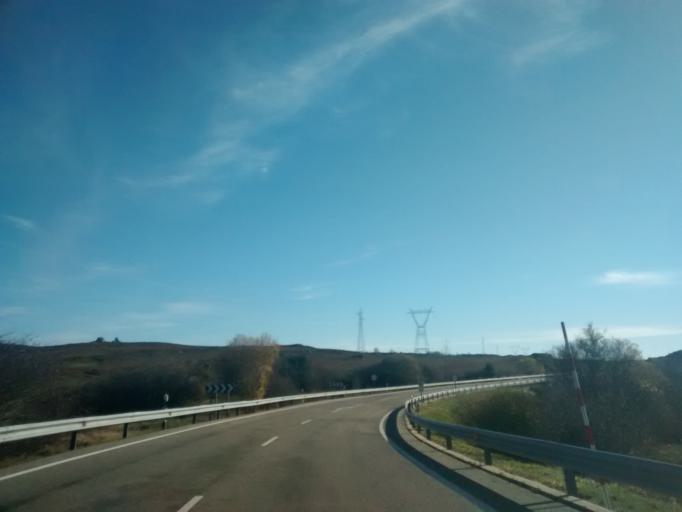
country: ES
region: Castille and Leon
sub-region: Provincia de Burgos
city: Arija
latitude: 42.9913
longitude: -3.8222
